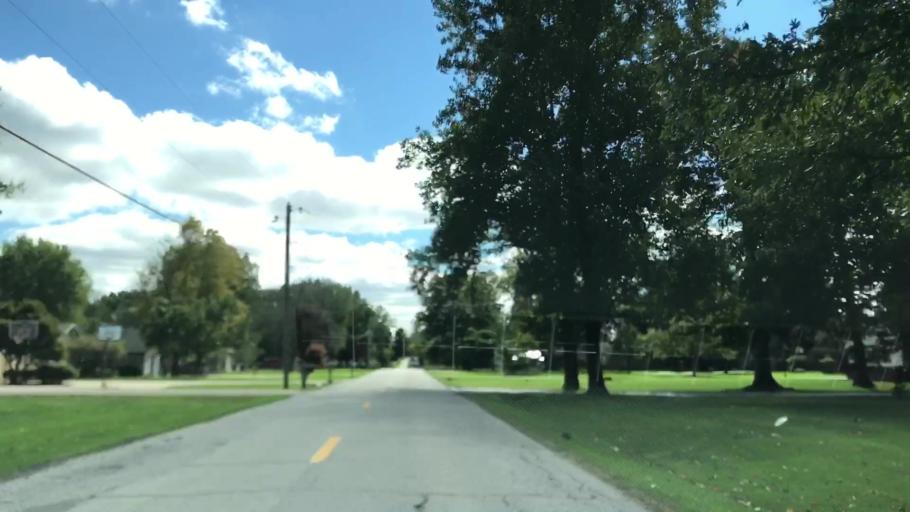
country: US
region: Indiana
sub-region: Howard County
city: Indian Heights
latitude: 40.4317
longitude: -86.1013
